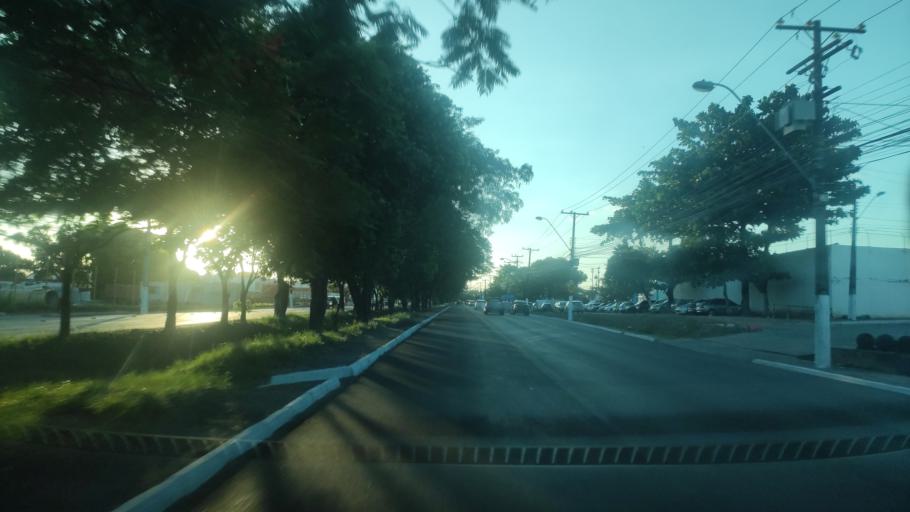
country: BR
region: Alagoas
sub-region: Satuba
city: Satuba
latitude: -9.5928
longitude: -35.7556
